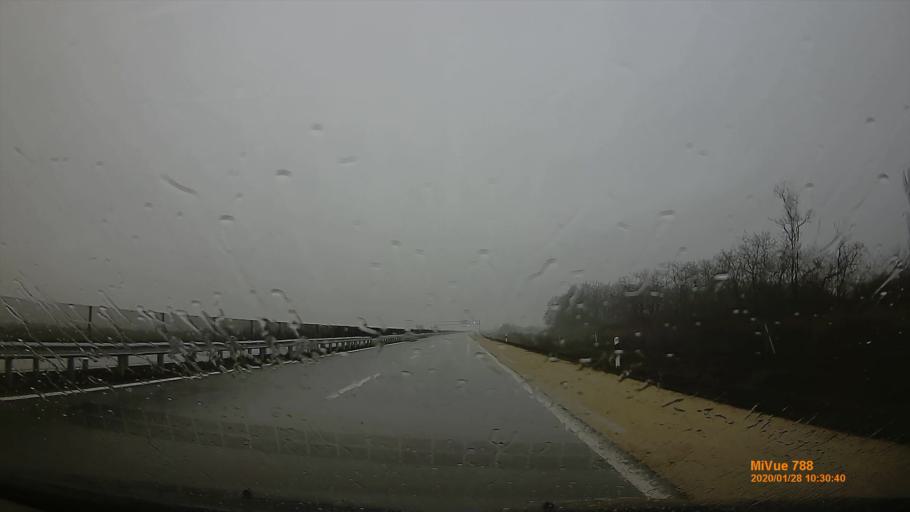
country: HU
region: Pest
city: Gomba
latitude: 47.3333
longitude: 19.5149
